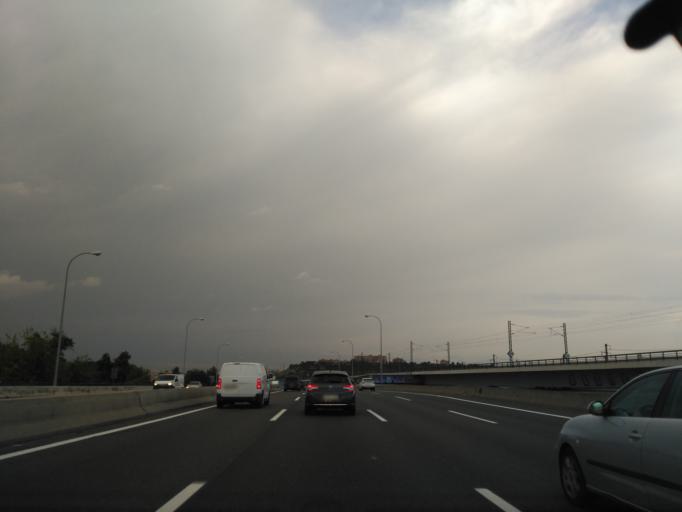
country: ES
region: Madrid
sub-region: Provincia de Madrid
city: Villaverde
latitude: 40.3662
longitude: -3.6780
